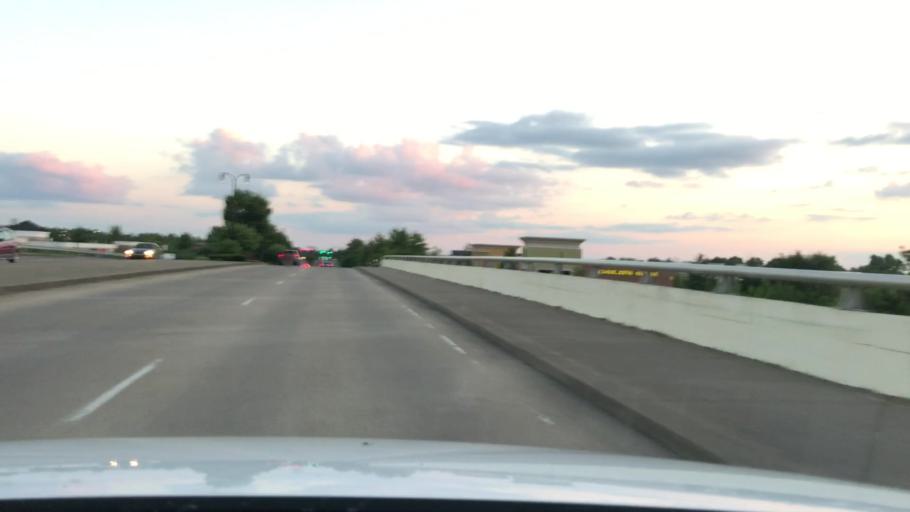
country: US
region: Tennessee
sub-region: Sumner County
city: Hendersonville
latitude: 36.3240
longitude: -86.5978
